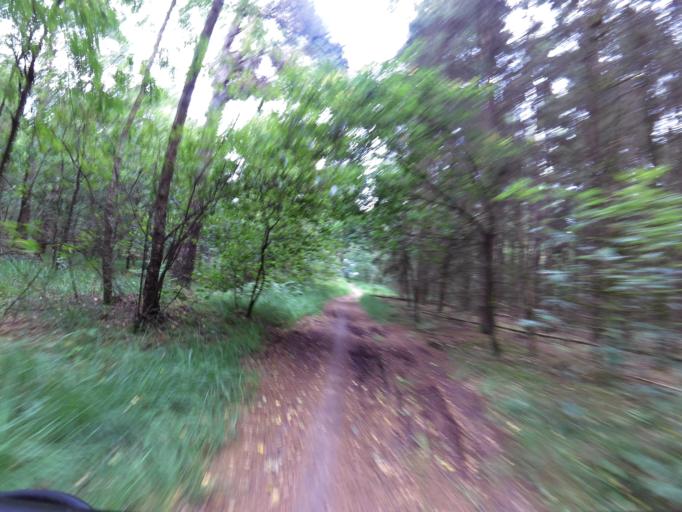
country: NL
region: North Brabant
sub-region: Gemeente Son en Breugel
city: Breugel
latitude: 51.5528
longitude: 5.5212
